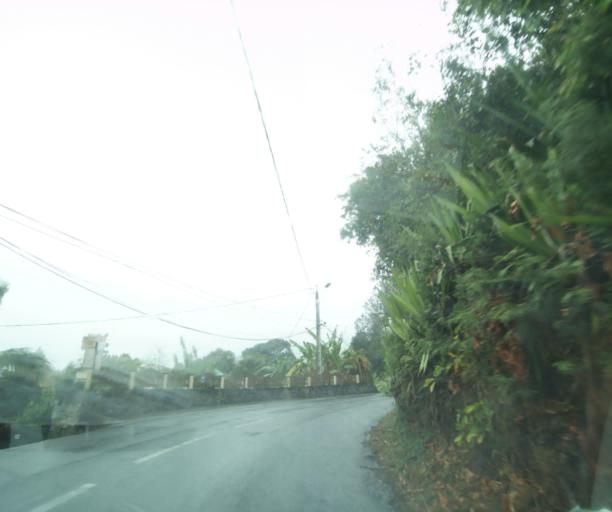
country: RE
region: Reunion
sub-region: Reunion
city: Saint-Paul
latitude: -21.0141
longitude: 55.3086
